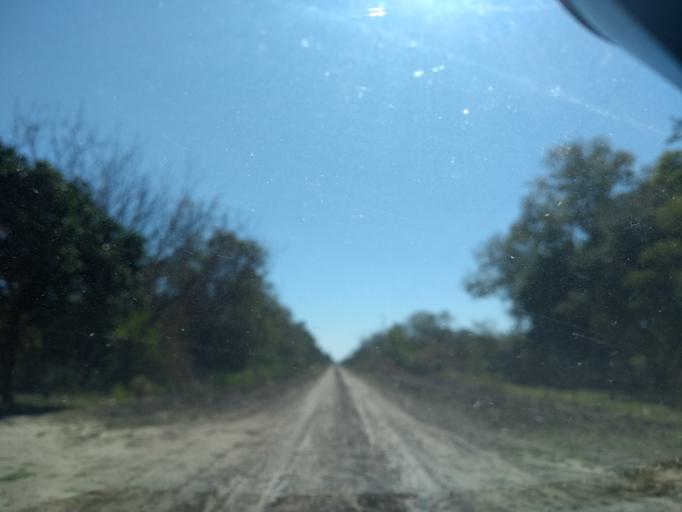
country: AR
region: Chaco
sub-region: Departamento de Quitilipi
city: Quitilipi
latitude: -26.7556
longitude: -60.2426
